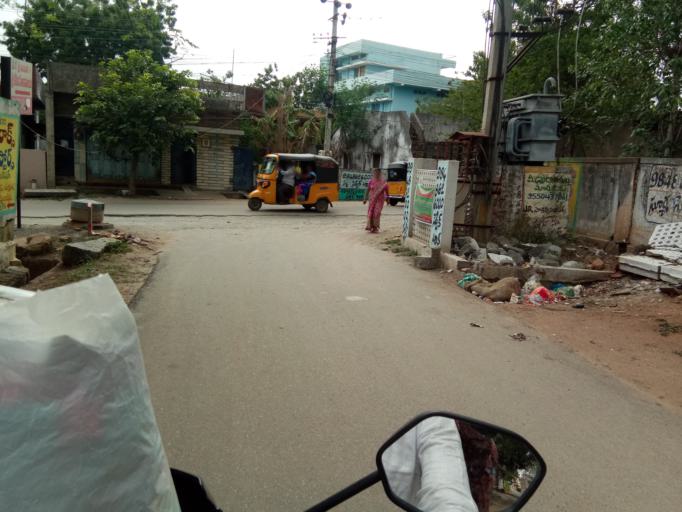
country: IN
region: Telangana
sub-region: Khammam
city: Khammam
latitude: 17.2375
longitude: 80.1459
